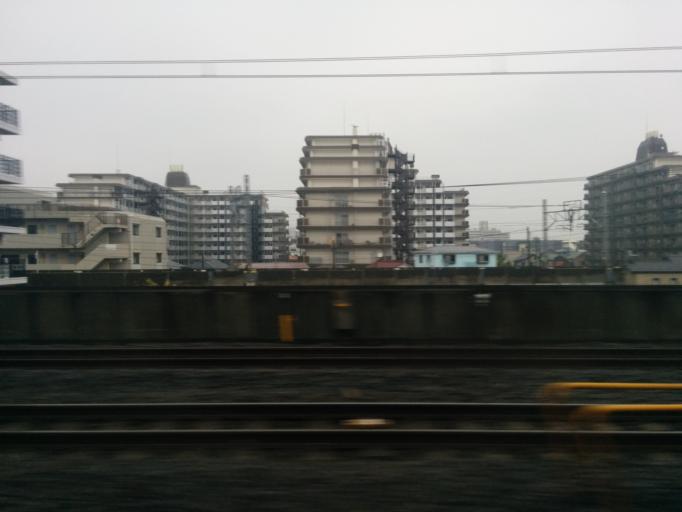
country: JP
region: Chiba
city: Funabashi
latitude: 35.7106
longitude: 139.9524
